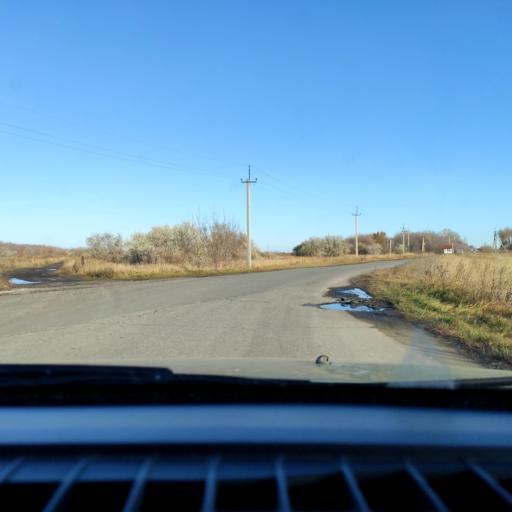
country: RU
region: Samara
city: Tol'yatti
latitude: 53.6574
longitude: 49.3315
